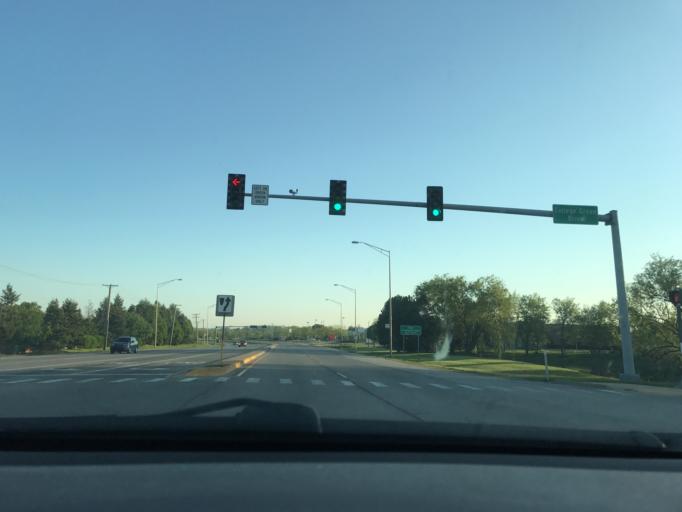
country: US
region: Illinois
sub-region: Kane County
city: South Elgin
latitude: 42.0147
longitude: -88.3363
